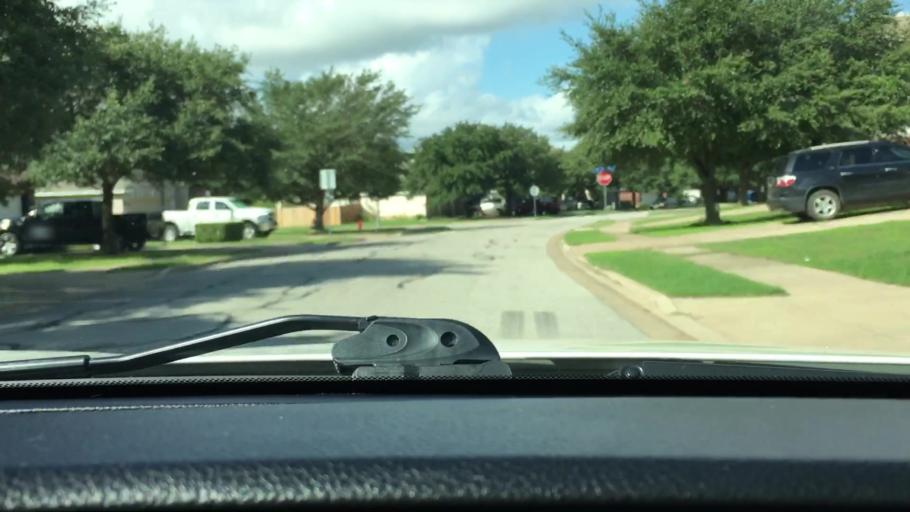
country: US
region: Texas
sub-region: Travis County
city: Windemere
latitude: 30.4760
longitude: -97.6453
